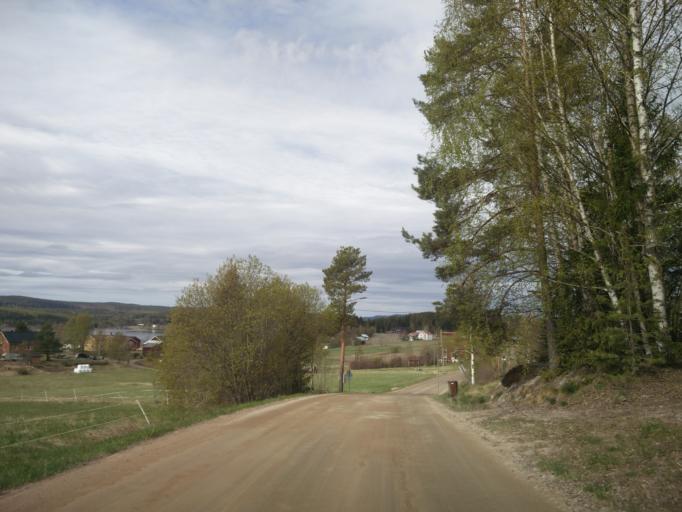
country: SE
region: Vaesternorrland
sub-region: Sundsvalls Kommun
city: Vi
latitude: 62.2781
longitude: 17.1273
